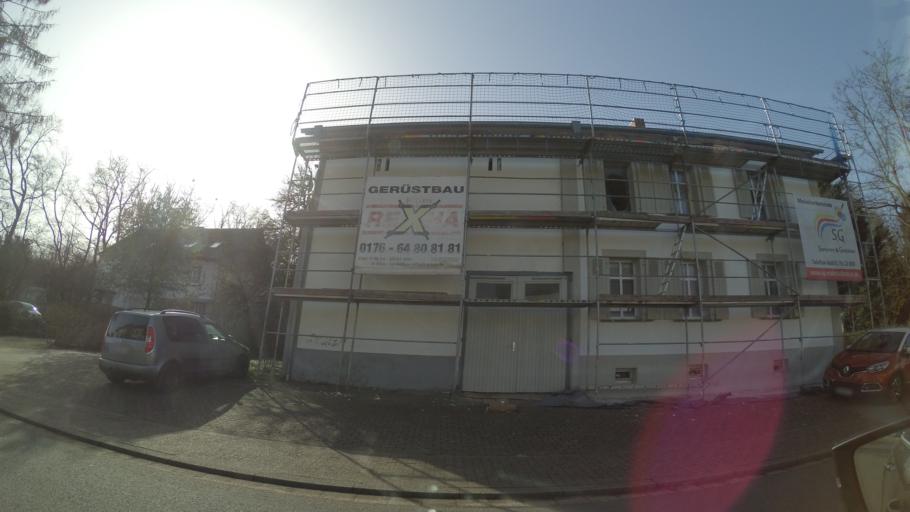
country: DE
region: Saarland
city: Wallerfangen
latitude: 49.3095
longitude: 6.7244
